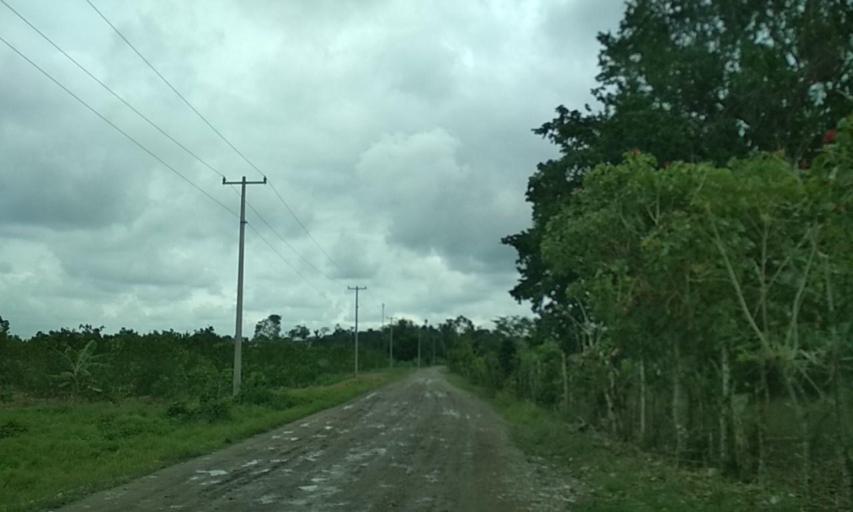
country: MX
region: Puebla
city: Espinal
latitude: 20.3205
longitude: -97.4233
